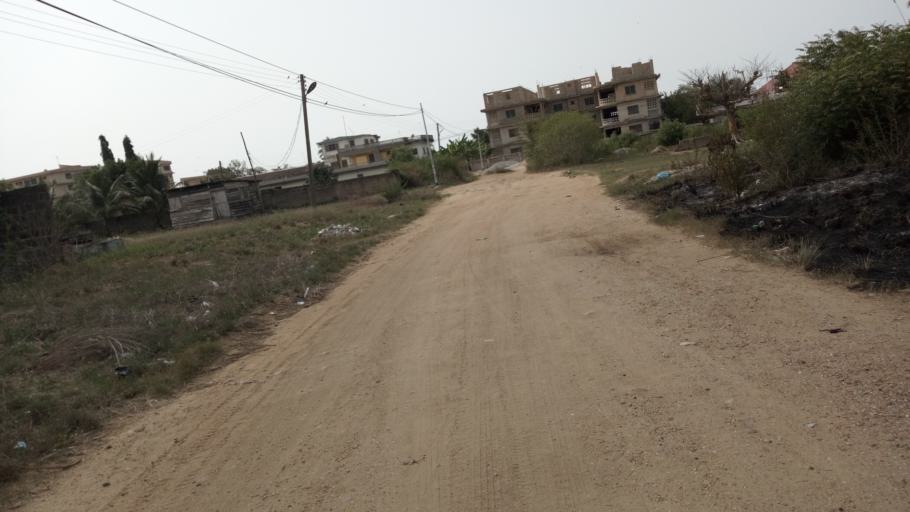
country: GH
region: Central
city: Winneba
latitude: 5.3684
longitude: -0.6404
